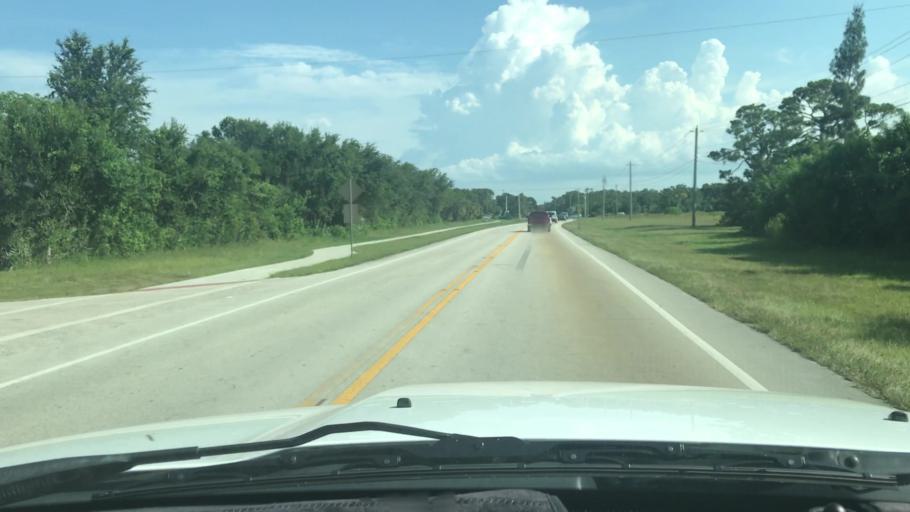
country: US
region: Florida
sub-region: Indian River County
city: Gifford
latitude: 27.6493
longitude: -80.4301
